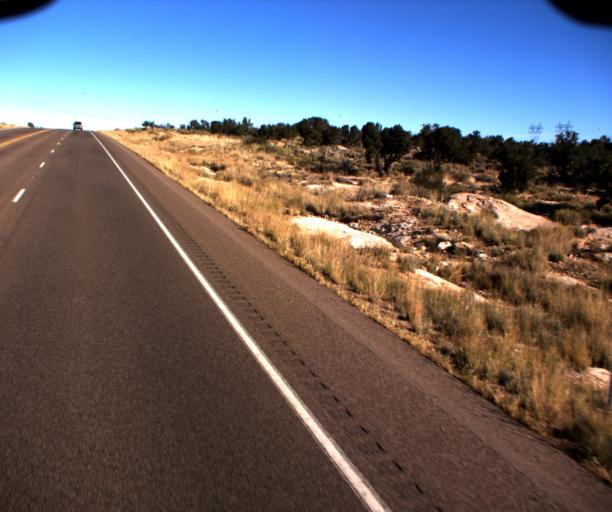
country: US
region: Arizona
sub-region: Navajo County
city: Snowflake
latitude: 34.6288
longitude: -110.0937
